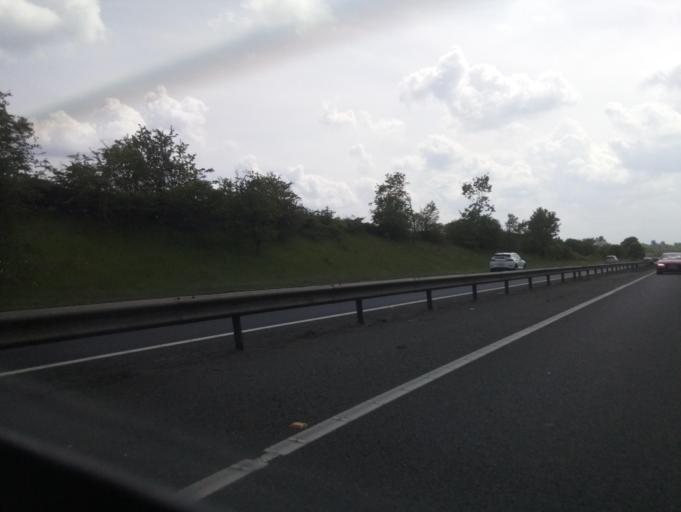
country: GB
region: England
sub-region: North Yorkshire
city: Thirsk
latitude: 54.2991
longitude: -1.3369
